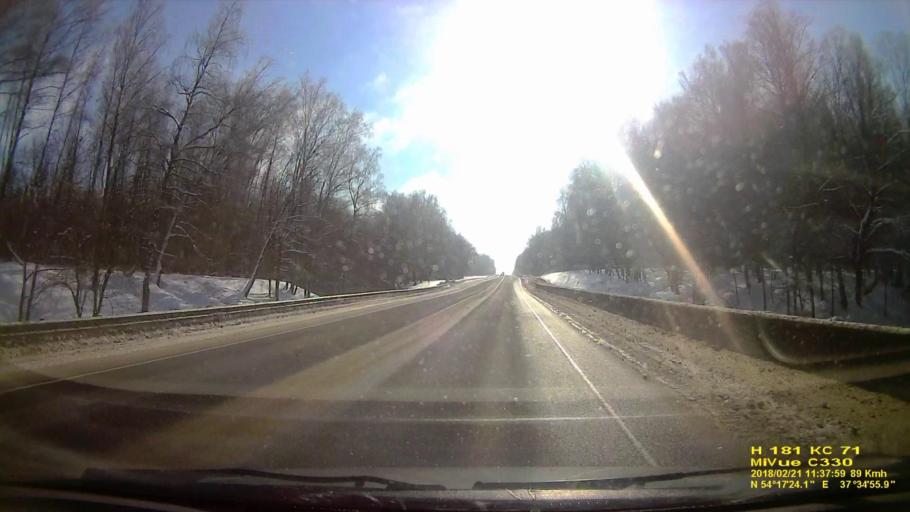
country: RU
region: Tula
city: Gorelki
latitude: 54.2898
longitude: 37.5824
